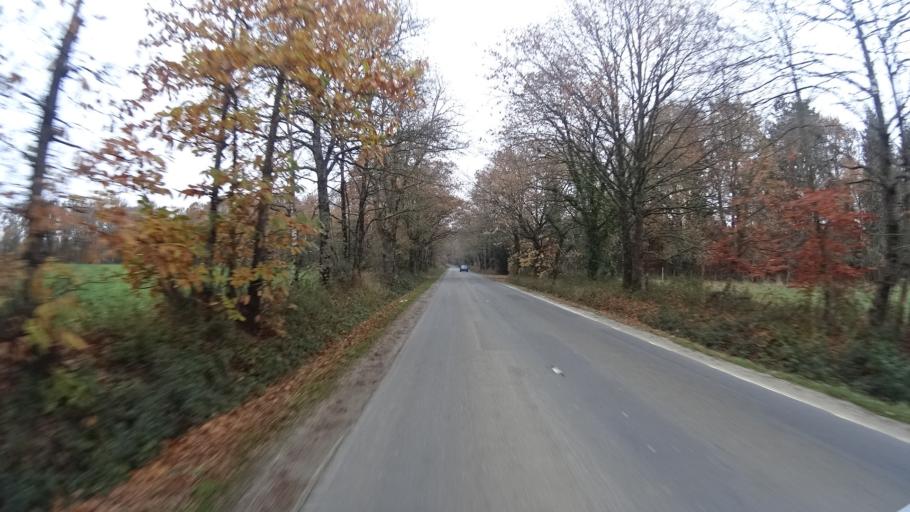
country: FR
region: Brittany
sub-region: Departement d'Ille-et-Vilaine
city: Bains-sur-Oust
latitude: 47.6982
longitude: -2.0562
